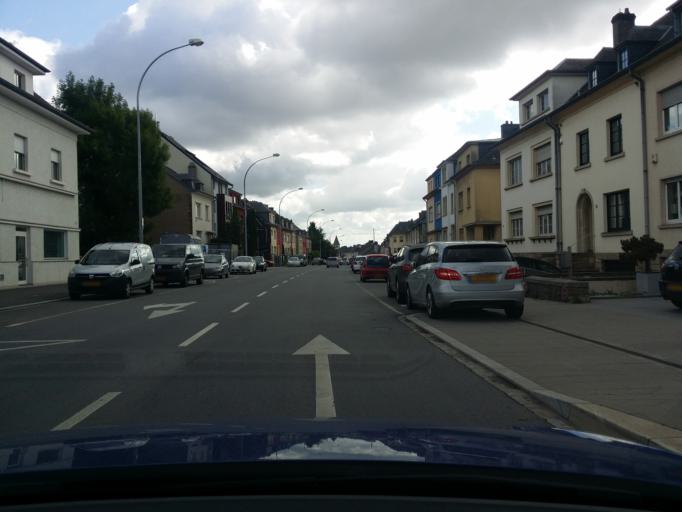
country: LU
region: Luxembourg
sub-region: Canton de Luxembourg
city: Strassen
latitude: 49.6035
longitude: 6.0849
